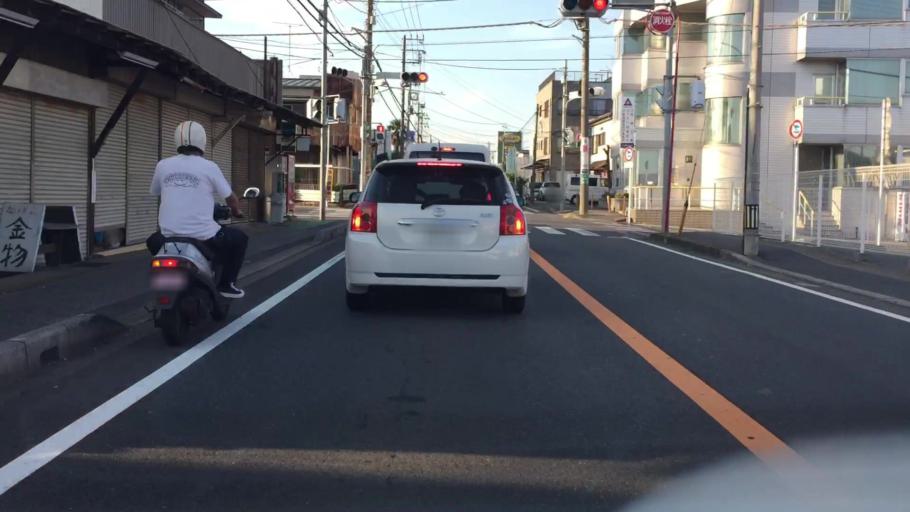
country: JP
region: Chiba
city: Funabashi
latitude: 35.7556
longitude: 139.9987
